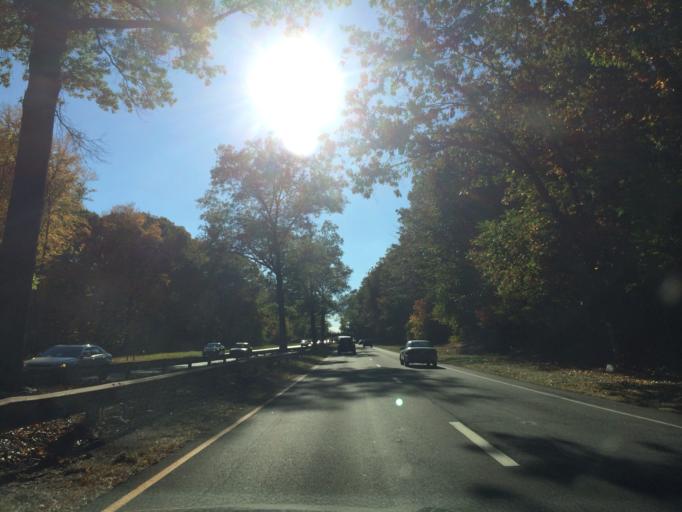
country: US
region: Connecticut
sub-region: Fairfield County
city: Norwalk
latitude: 41.1476
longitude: -73.4139
